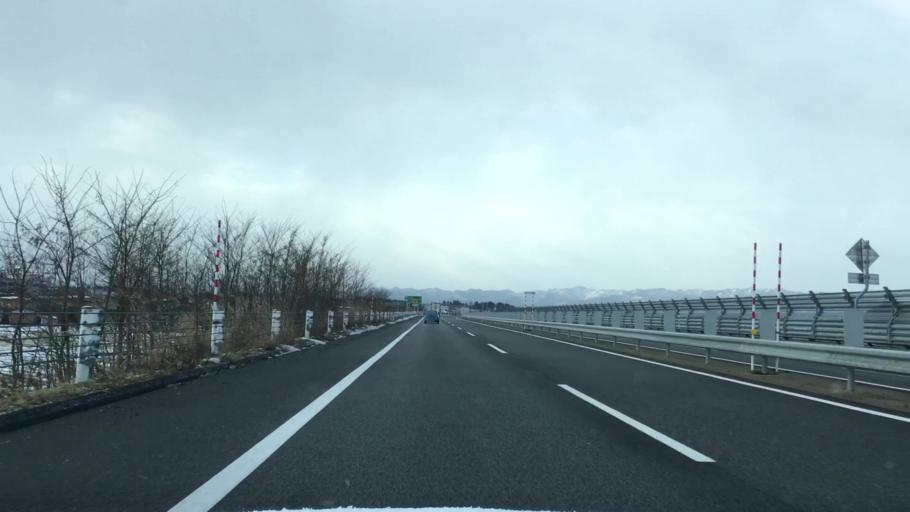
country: JP
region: Akita
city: Odate
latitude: 40.2960
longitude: 140.5538
